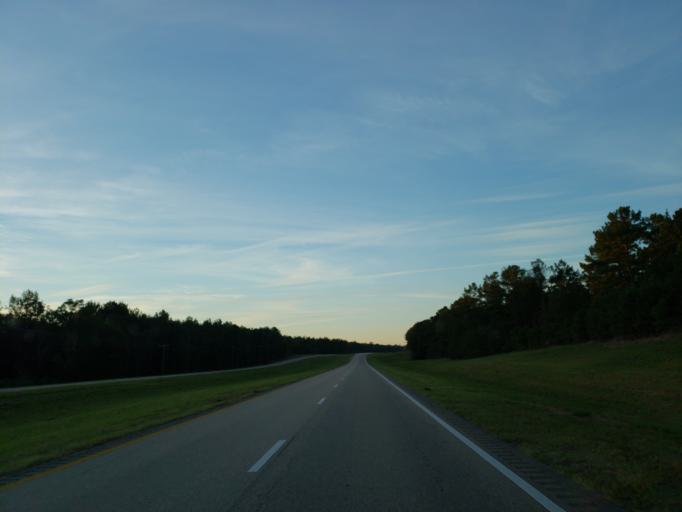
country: US
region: Mississippi
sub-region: Wayne County
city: Belmont
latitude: 31.4865
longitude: -88.4886
